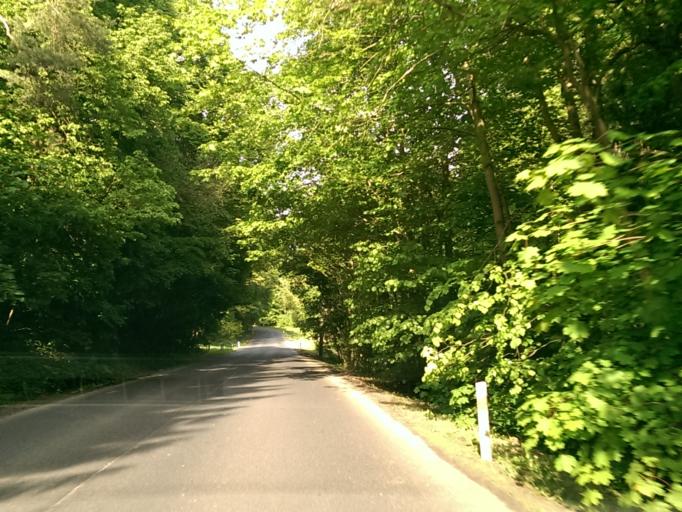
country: CZ
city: Duba
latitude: 50.5490
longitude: 14.5666
